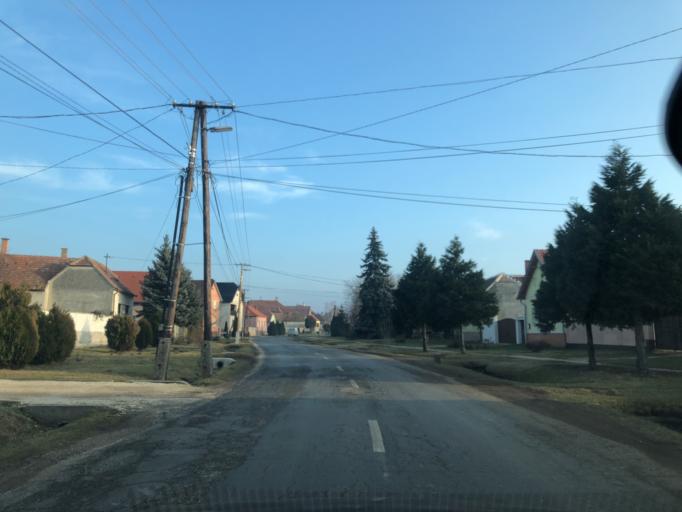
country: HU
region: Gyor-Moson-Sopron
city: Kapuvar
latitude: 47.6007
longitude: 17.0847
